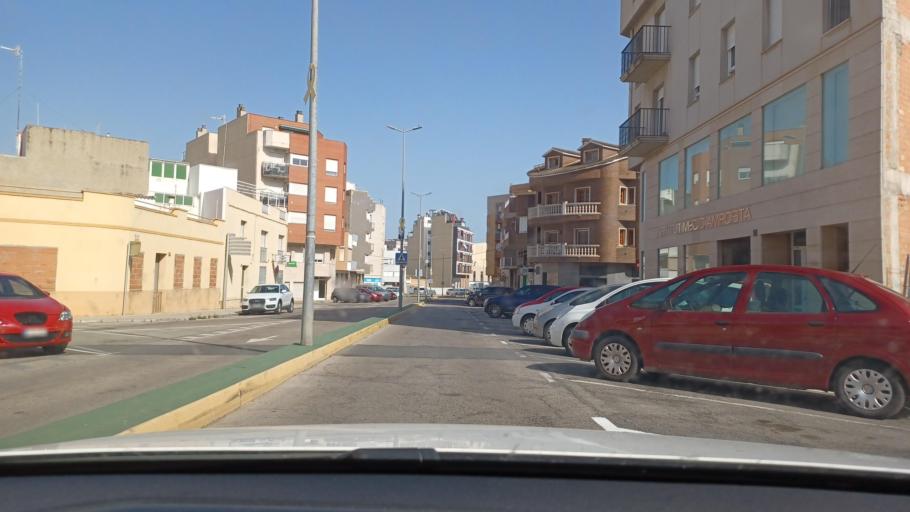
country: ES
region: Catalonia
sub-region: Provincia de Tarragona
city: Amposta
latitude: 40.7078
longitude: 0.5760
